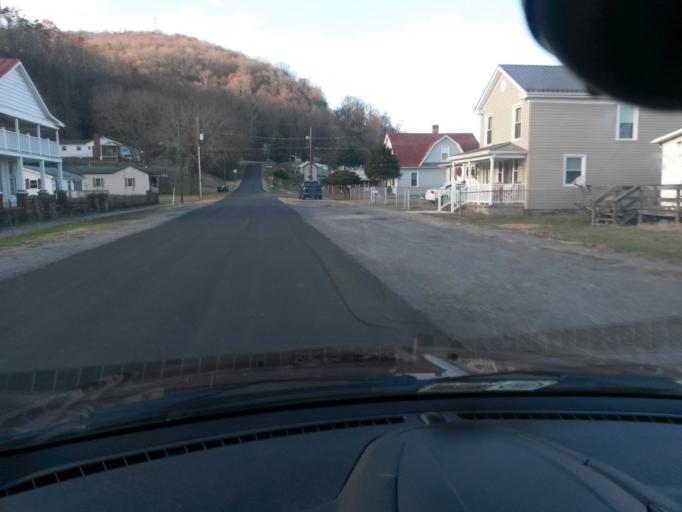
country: US
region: Virginia
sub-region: Alleghany County
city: Clifton Forge
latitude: 37.8008
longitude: -79.7927
